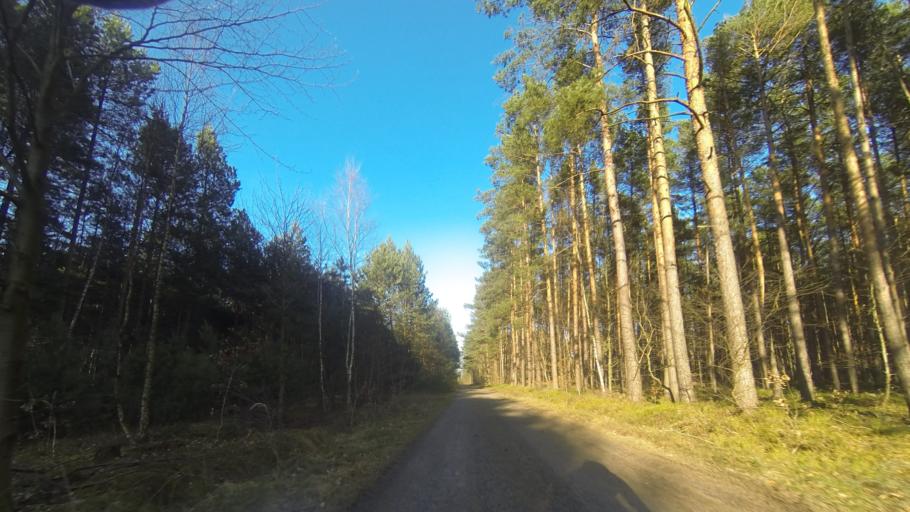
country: DE
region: Saxony
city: Tauscha
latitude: 51.2484
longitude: 13.8347
